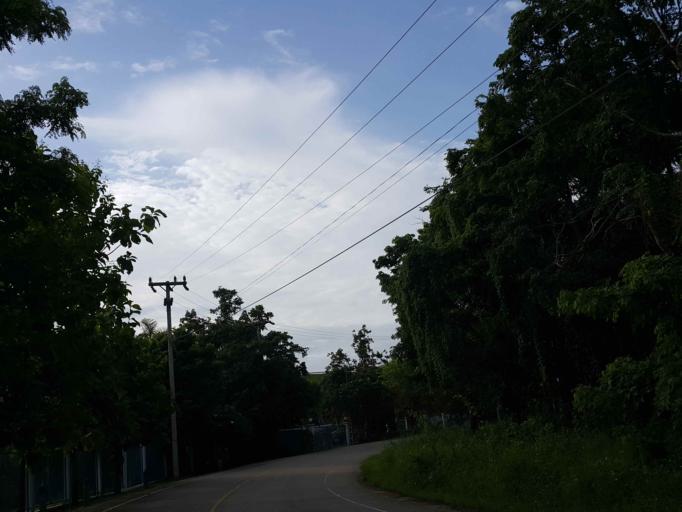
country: TH
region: Chiang Mai
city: San Sai
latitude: 18.9367
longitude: 99.1407
